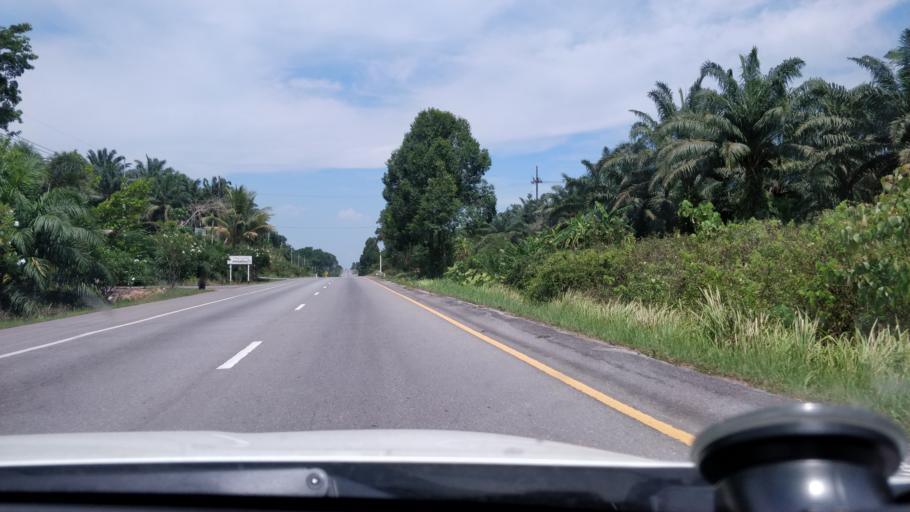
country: TH
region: Surat Thani
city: Chai Buri
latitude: 8.6425
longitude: 99.0396
